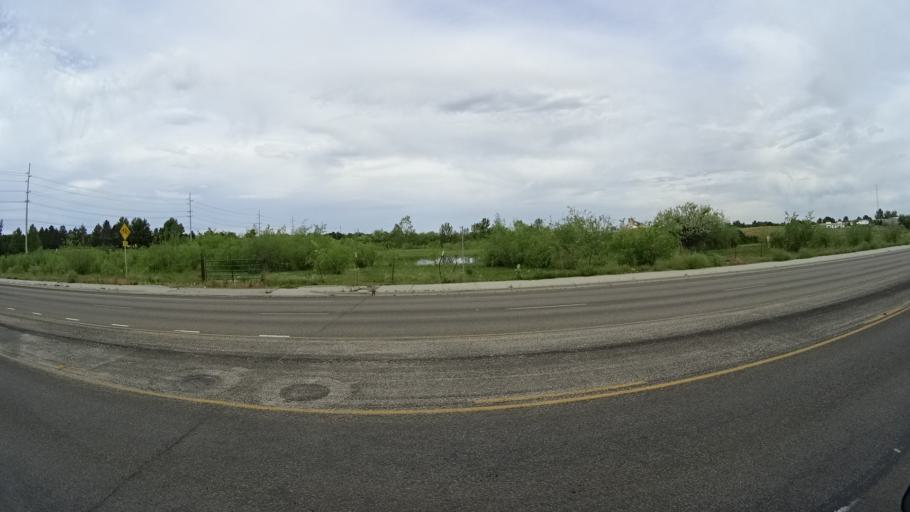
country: US
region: Idaho
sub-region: Ada County
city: Meridian
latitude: 43.6061
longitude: -116.3744
